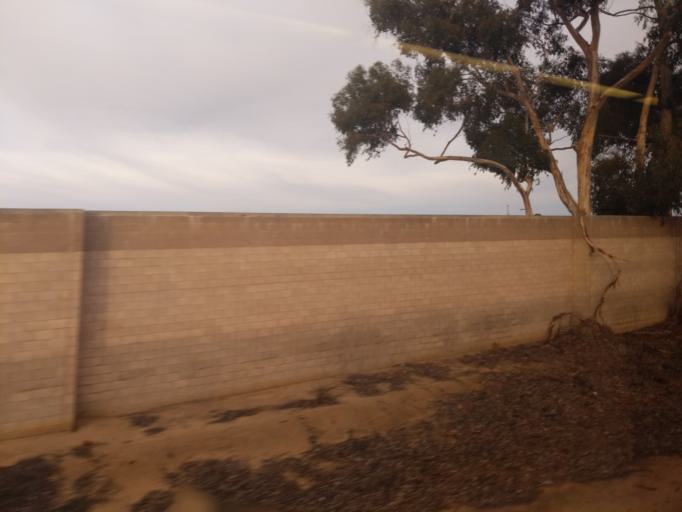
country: US
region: California
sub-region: San Diego County
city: Camp Pendleton South
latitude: 33.2143
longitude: -117.3911
